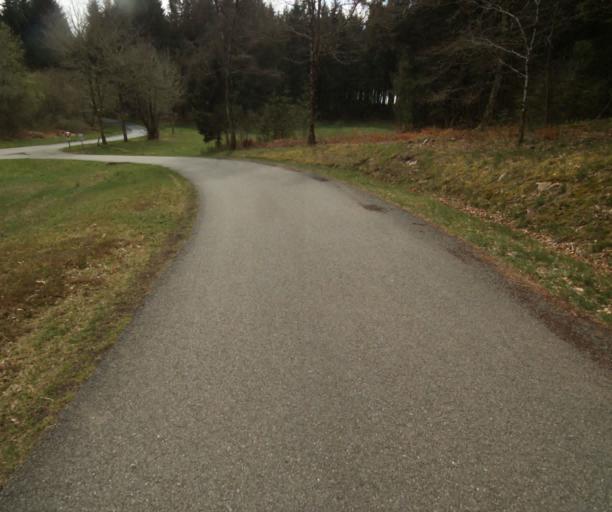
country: FR
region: Limousin
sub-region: Departement de la Correze
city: Egletons
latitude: 45.3373
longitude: 1.9785
